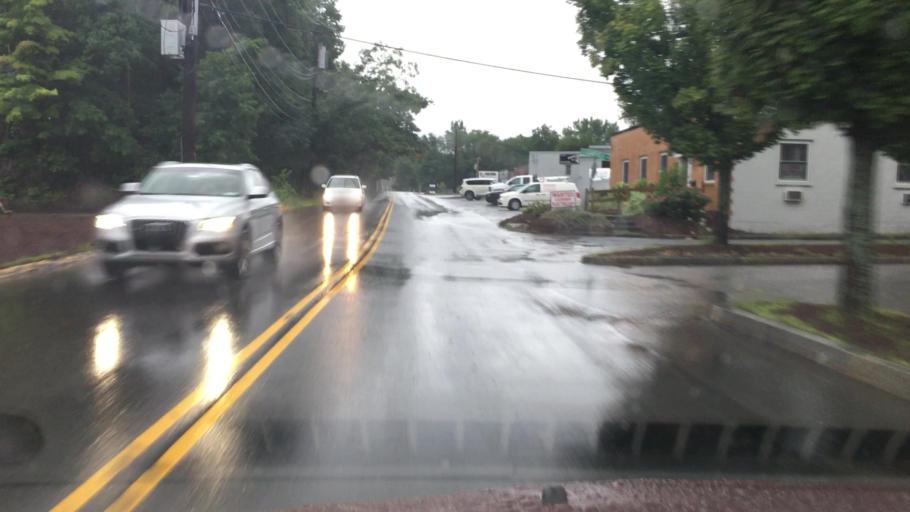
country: US
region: Massachusetts
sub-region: Middlesex County
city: Lexington
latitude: 42.4717
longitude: -71.2124
